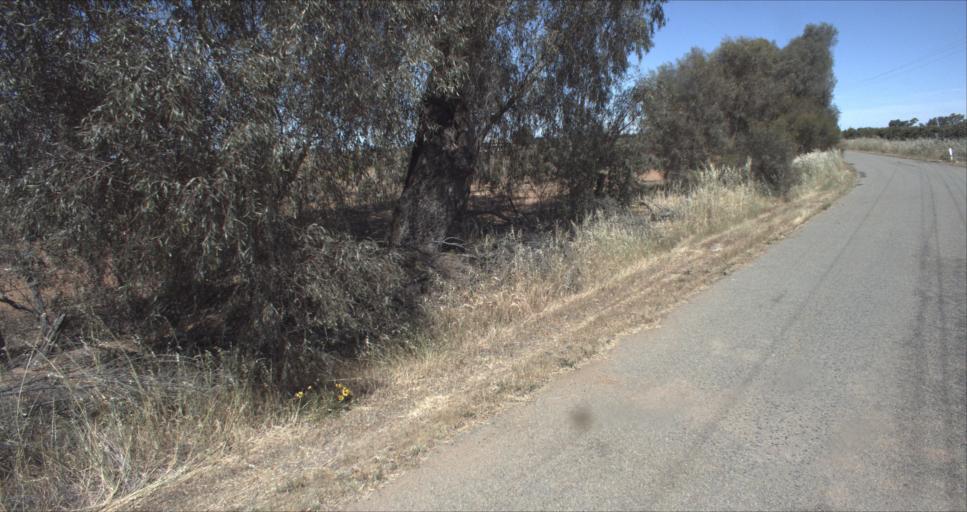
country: AU
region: New South Wales
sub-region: Leeton
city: Leeton
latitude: -34.5272
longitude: 146.3460
